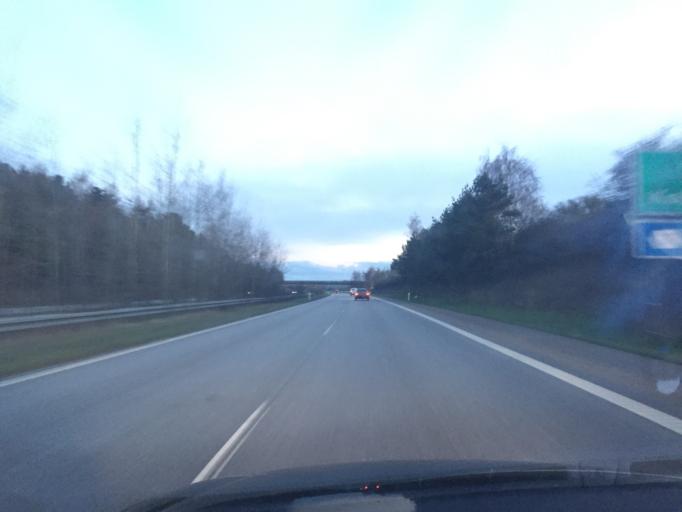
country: DK
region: Capital Region
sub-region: Fredensborg Kommune
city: Niva
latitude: 55.9578
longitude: 12.4814
